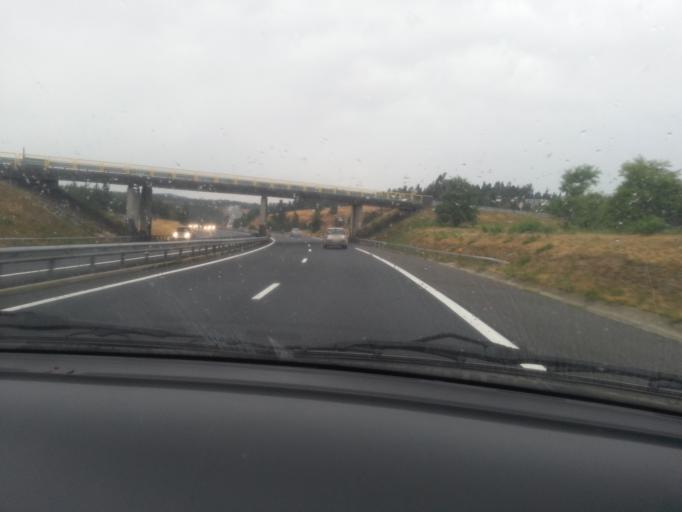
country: FR
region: Languedoc-Roussillon
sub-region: Departement de la Lozere
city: Aumont-Aubrac
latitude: 44.6995
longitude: 3.2822
